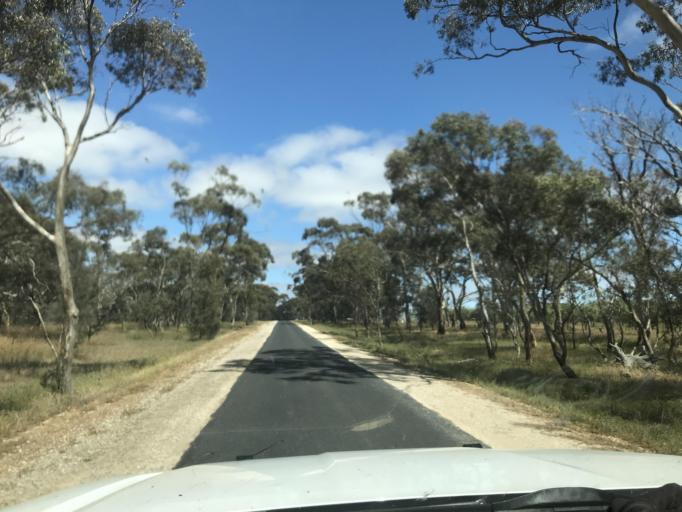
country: AU
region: South Australia
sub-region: Tatiara
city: Bordertown
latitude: -36.3064
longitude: 141.0658
